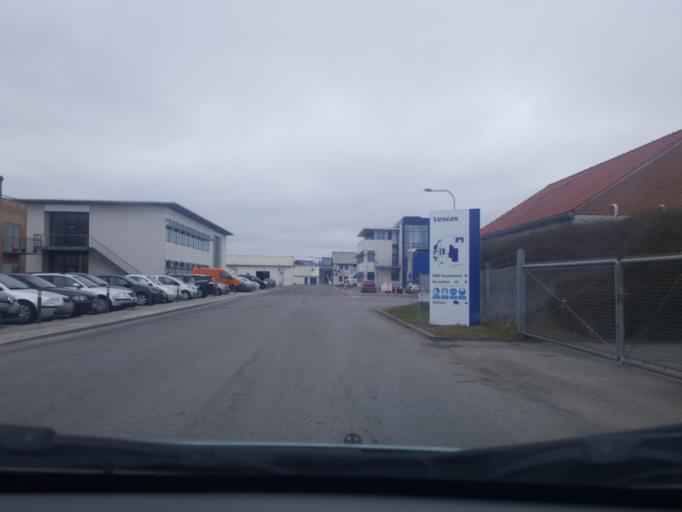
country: DK
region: Central Jutland
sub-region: Ringkobing-Skjern Kommune
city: Ringkobing
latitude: 56.0896
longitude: 8.2375
